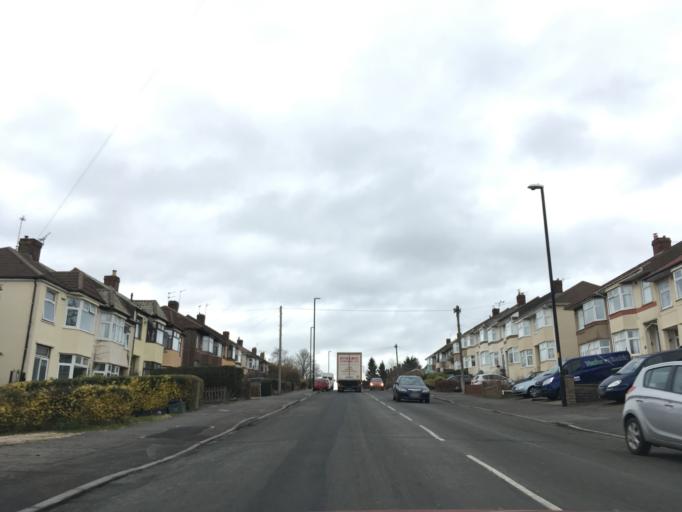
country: GB
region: England
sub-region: Bristol
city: Bristol
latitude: 51.4809
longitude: -2.5730
